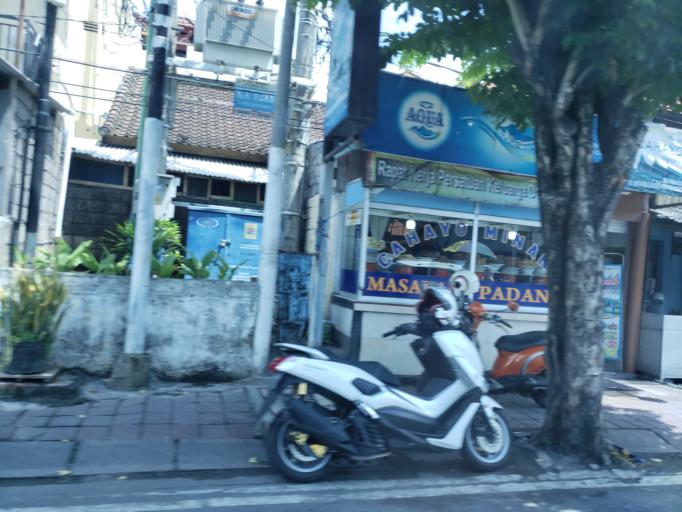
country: ID
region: Bali
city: Jimbaran
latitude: -8.7739
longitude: 115.1721
